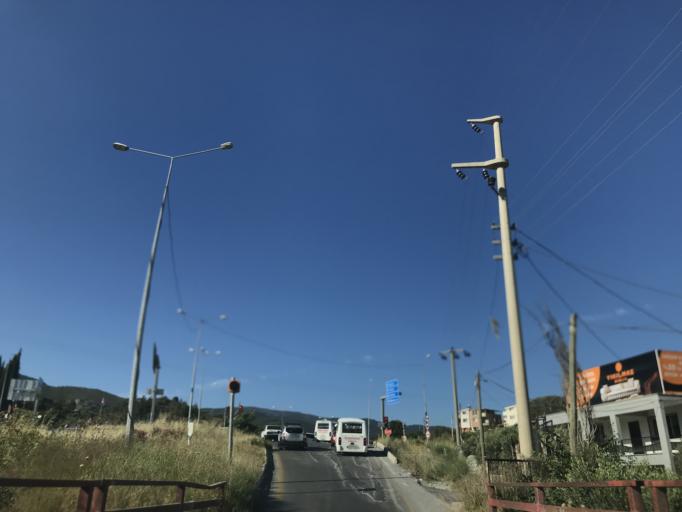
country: TR
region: Aydin
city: Soeke
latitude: 37.7608
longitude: 27.3768
